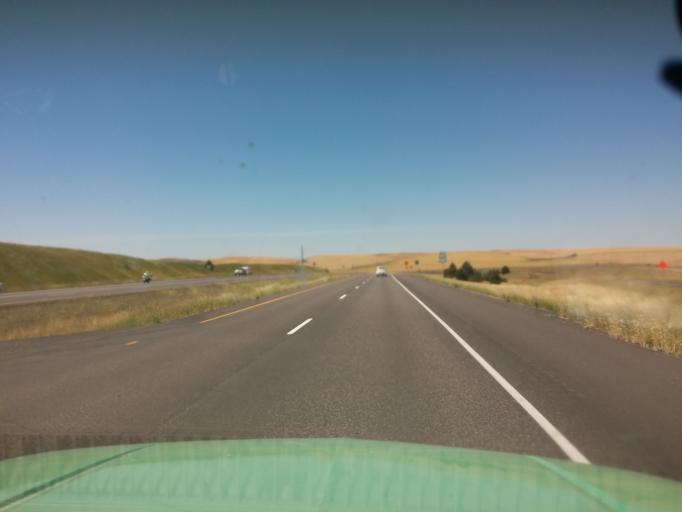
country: US
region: Washington
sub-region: Asotin County
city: Clarkston
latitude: 46.4705
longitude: -117.0322
